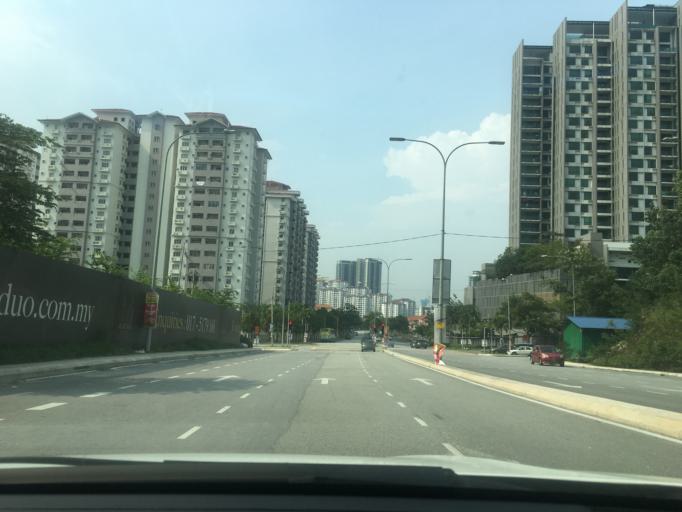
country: MY
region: Selangor
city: Kampong Baharu Balakong
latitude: 3.0545
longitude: 101.6717
